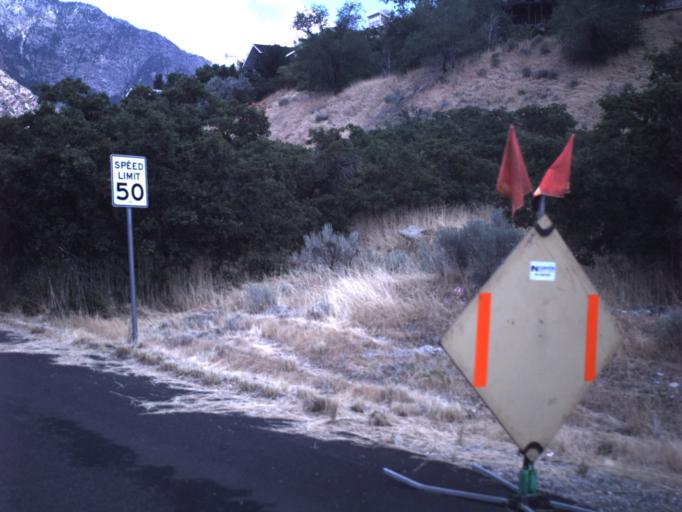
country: US
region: Utah
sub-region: Salt Lake County
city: Cottonwood Heights
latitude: 40.6113
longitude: -111.7908
